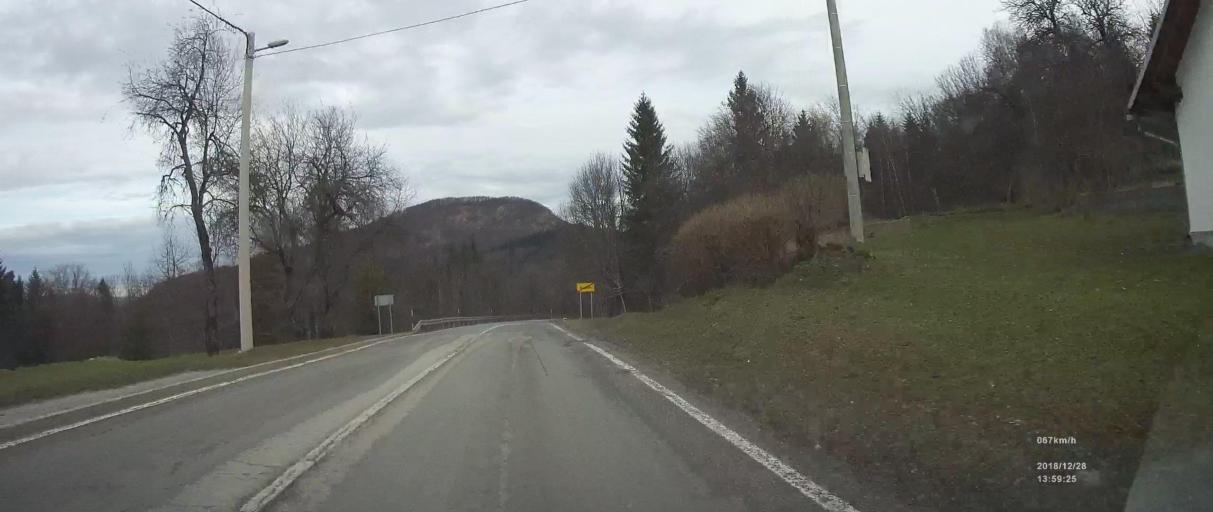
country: SI
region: Kostel
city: Kostel
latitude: 45.4024
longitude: 14.9098
